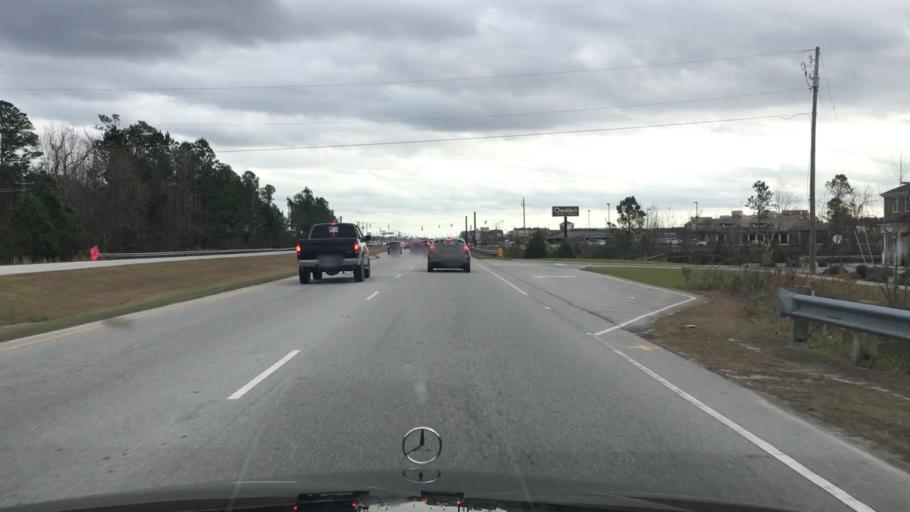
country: US
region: North Carolina
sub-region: Onslow County
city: Pumpkin Center
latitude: 34.7932
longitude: -77.4081
